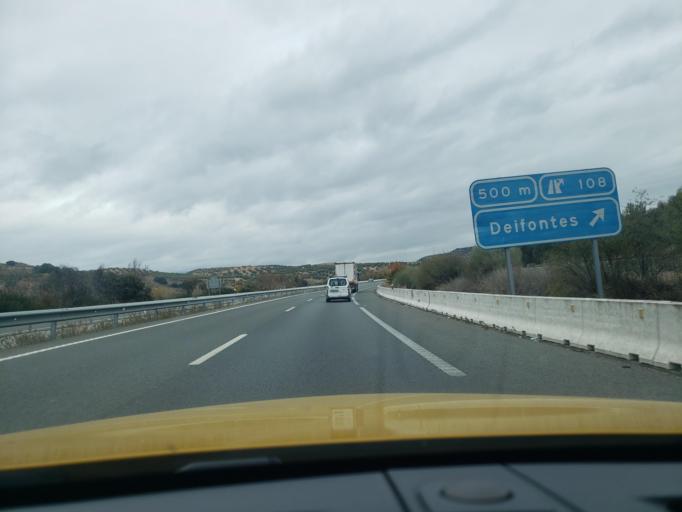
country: ES
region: Andalusia
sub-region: Provincia de Granada
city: Deifontes
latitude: 37.3185
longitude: -3.6433
